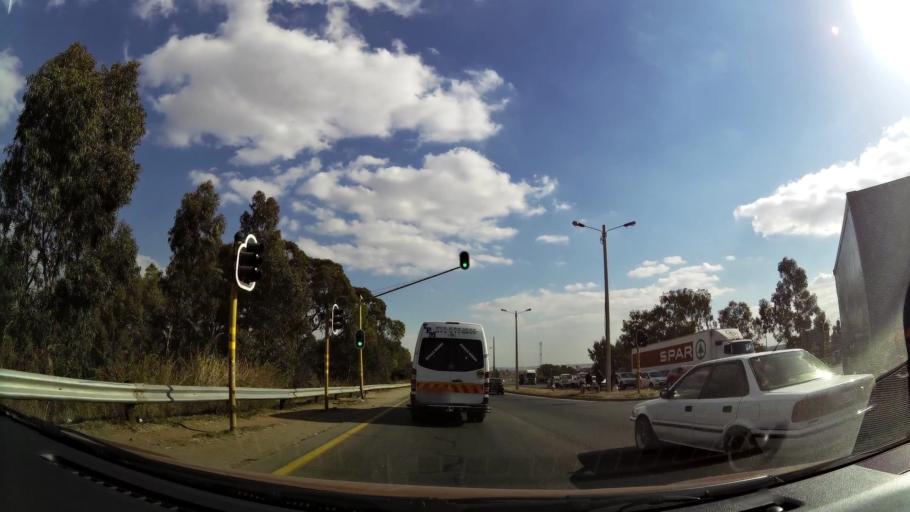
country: ZA
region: Gauteng
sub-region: Ekurhuleni Metropolitan Municipality
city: Tembisa
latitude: -25.9748
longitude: 28.2423
